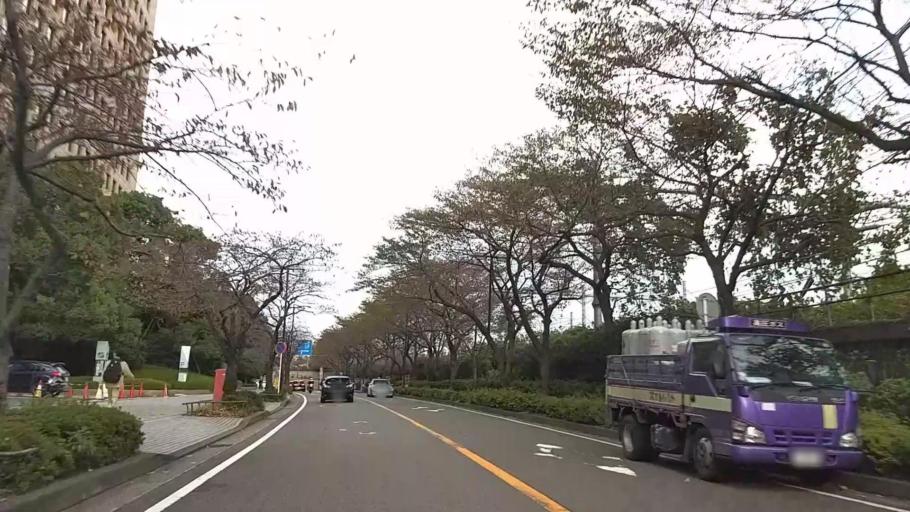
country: JP
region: Kanagawa
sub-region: Kawasaki-shi
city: Kawasaki
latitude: 35.5353
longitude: 139.7014
